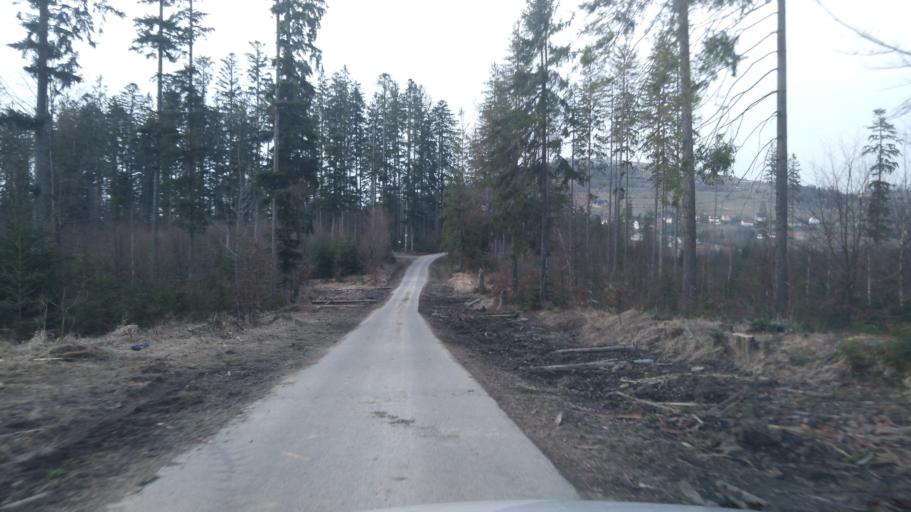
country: PL
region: Silesian Voivodeship
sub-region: Powiat cieszynski
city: Koniakow
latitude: 49.5303
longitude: 18.9508
